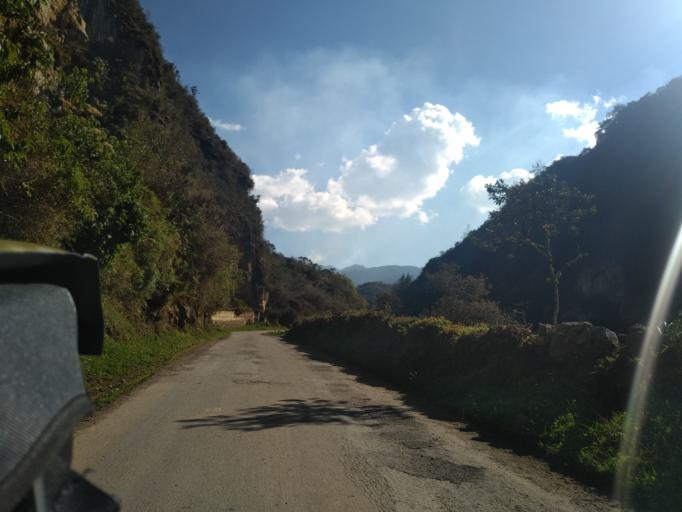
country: PE
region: Amazonas
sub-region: Provincia de Chachapoyas
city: Montevideo
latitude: -6.7248
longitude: -77.8258
